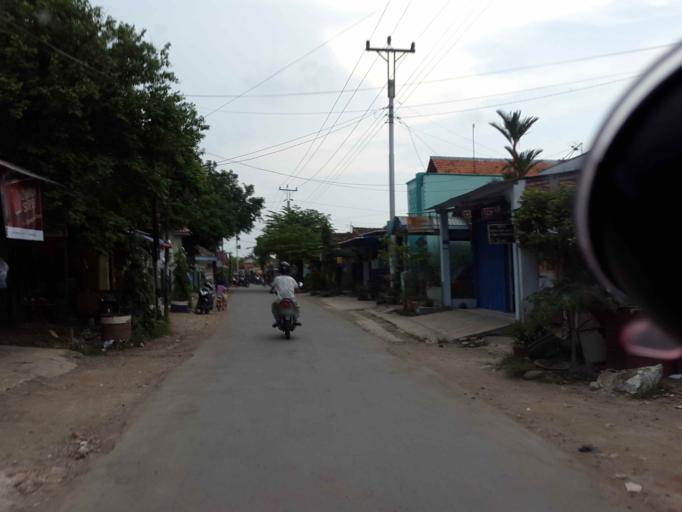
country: ID
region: Central Java
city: Pemalang
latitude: -6.8949
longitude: 109.3781
